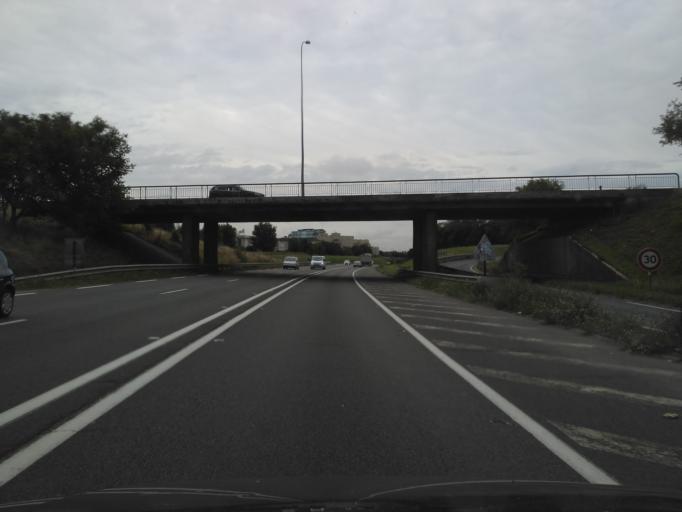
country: FR
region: Ile-de-France
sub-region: Departement de Seine-et-Marne
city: Rubelles
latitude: 48.5526
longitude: 2.6673
